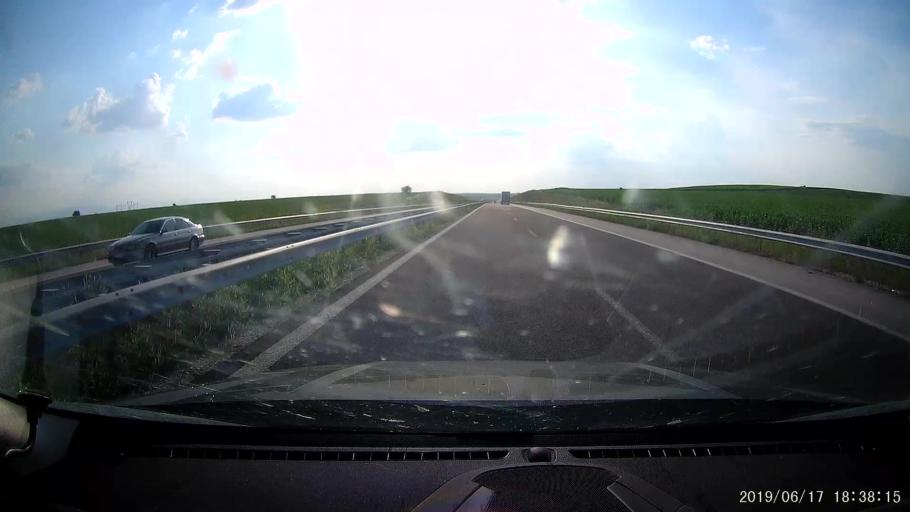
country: BG
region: Stara Zagora
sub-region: Obshtina Chirpan
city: Chirpan
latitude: 42.1359
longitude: 25.3417
